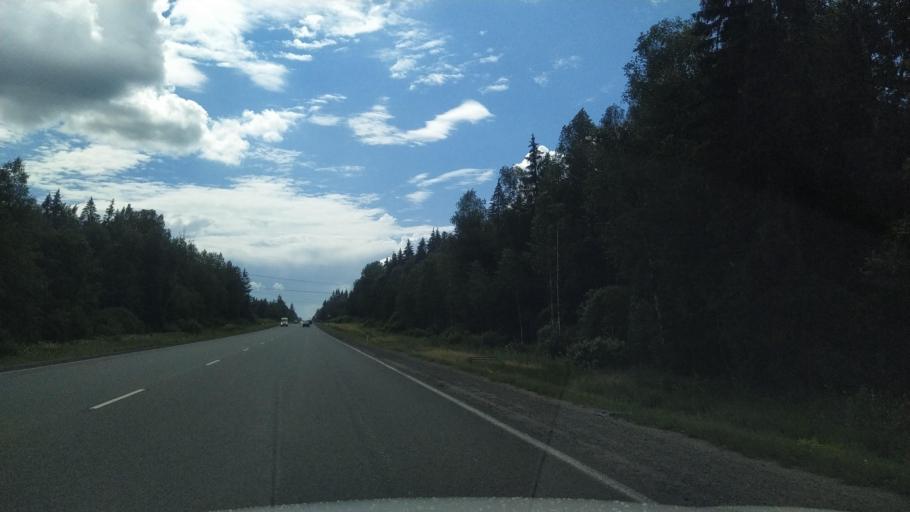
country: RU
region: Leningrad
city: Rozhdestveno
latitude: 59.3983
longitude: 29.9728
